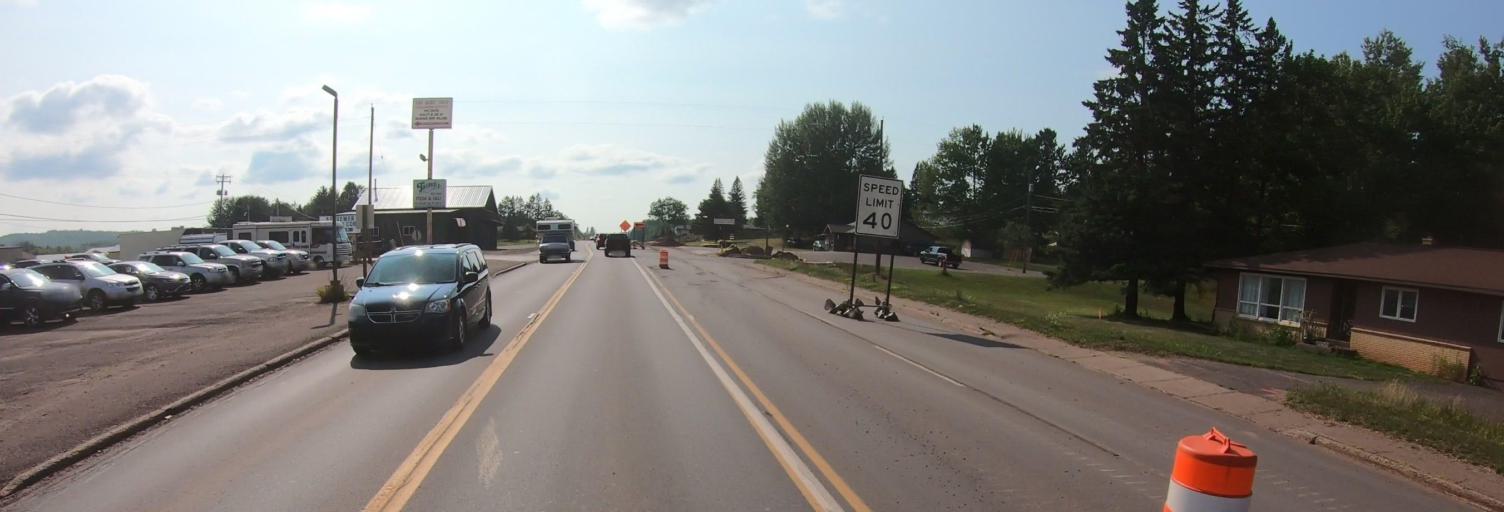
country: US
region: Michigan
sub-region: Gogebic County
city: Bessemer
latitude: 46.4812
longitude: -90.0605
